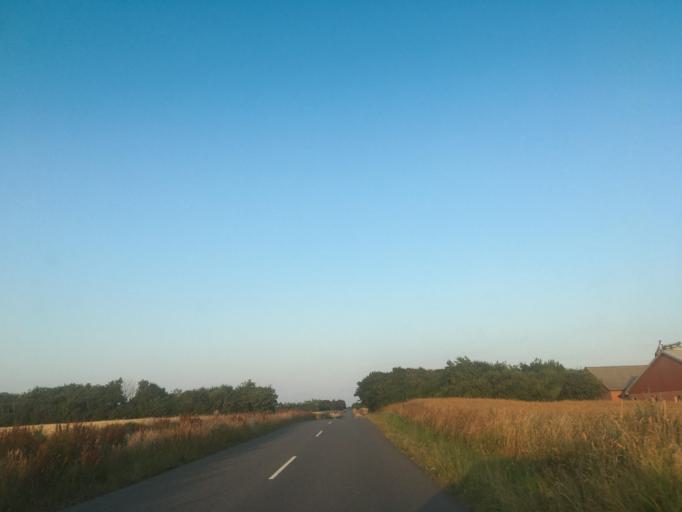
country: DK
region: North Denmark
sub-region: Thisted Kommune
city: Hurup
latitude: 56.7555
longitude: 8.3670
